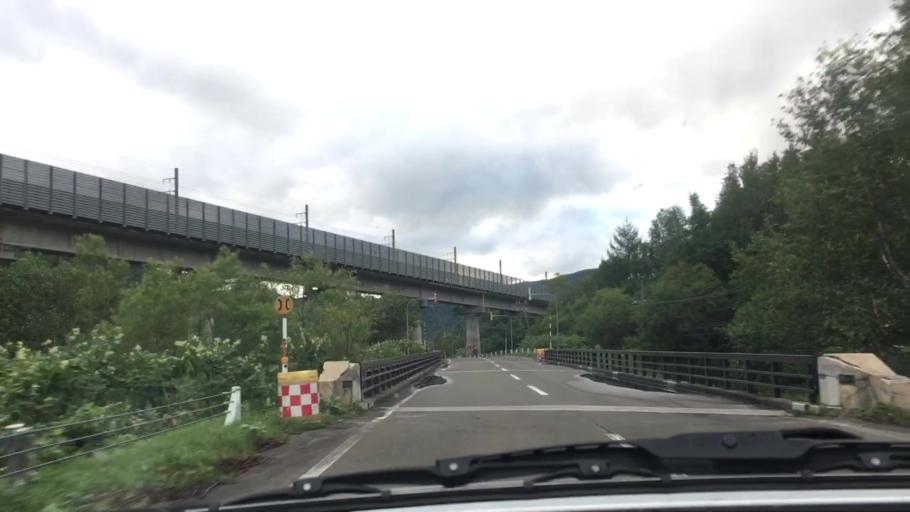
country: JP
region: Hokkaido
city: Shimo-furano
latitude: 43.0591
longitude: 142.5641
